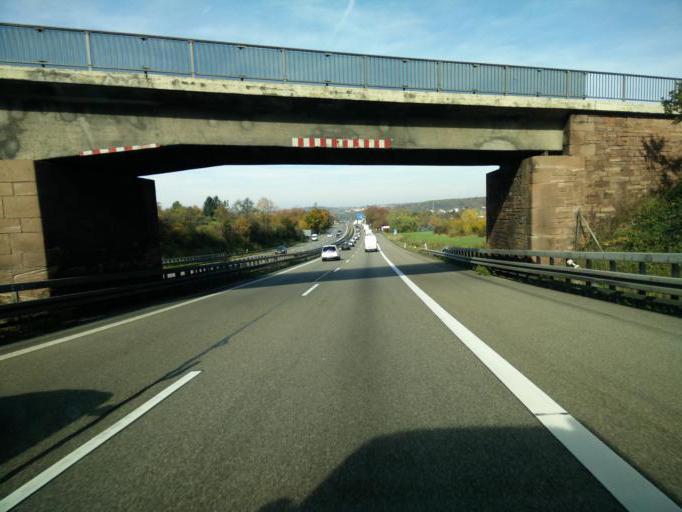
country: DE
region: Baden-Wuerttemberg
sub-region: Karlsruhe Region
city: Niefern-Oschelbronn
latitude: 48.9018
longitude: 8.7797
